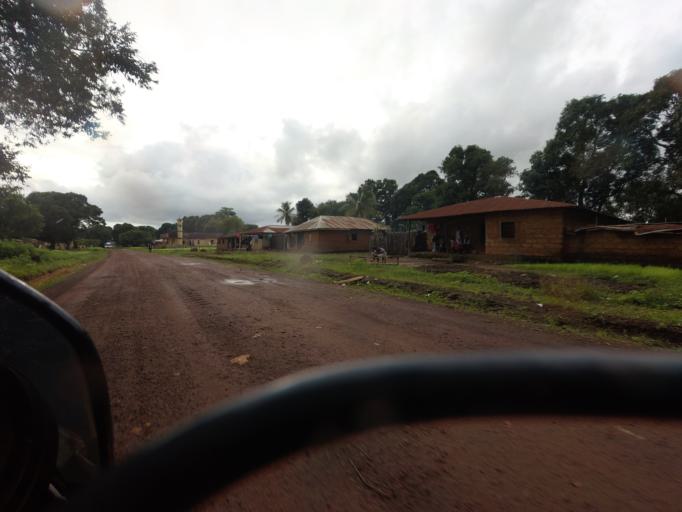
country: SL
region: Northern Province
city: Kambia
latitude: 9.2271
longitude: -12.8172
